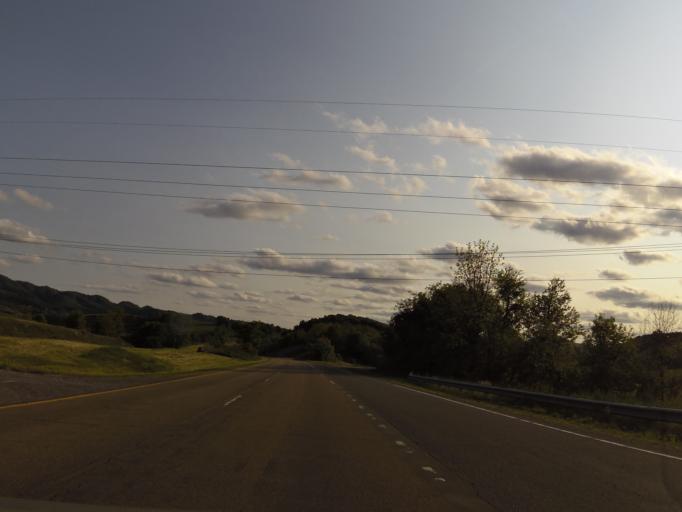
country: US
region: Virginia
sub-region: Tazewell County
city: Tazewell
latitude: 37.1399
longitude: -81.5127
